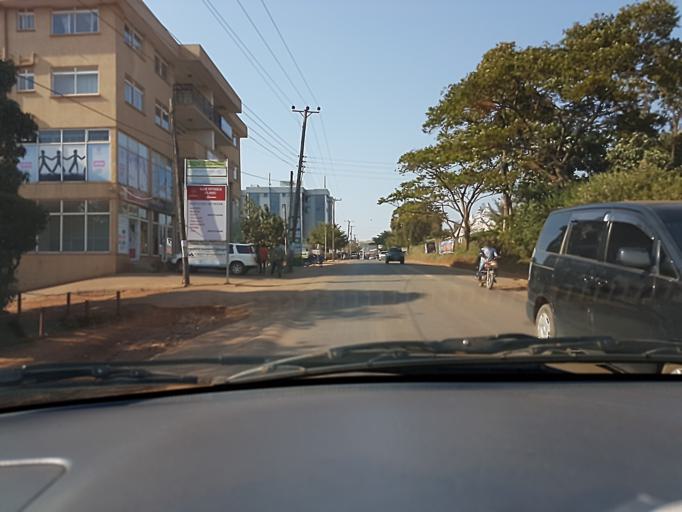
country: UG
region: Central Region
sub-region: Wakiso District
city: Kireka
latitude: 0.3516
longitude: 32.6155
